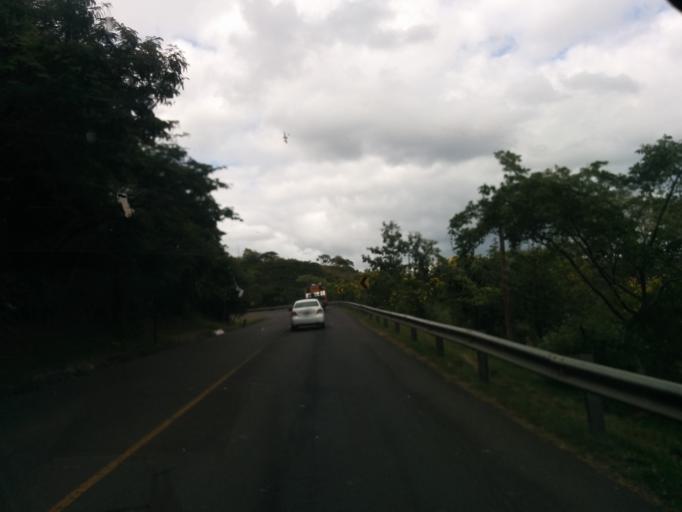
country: NI
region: Esteli
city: Esteli
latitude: 12.9971
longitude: -86.2841
